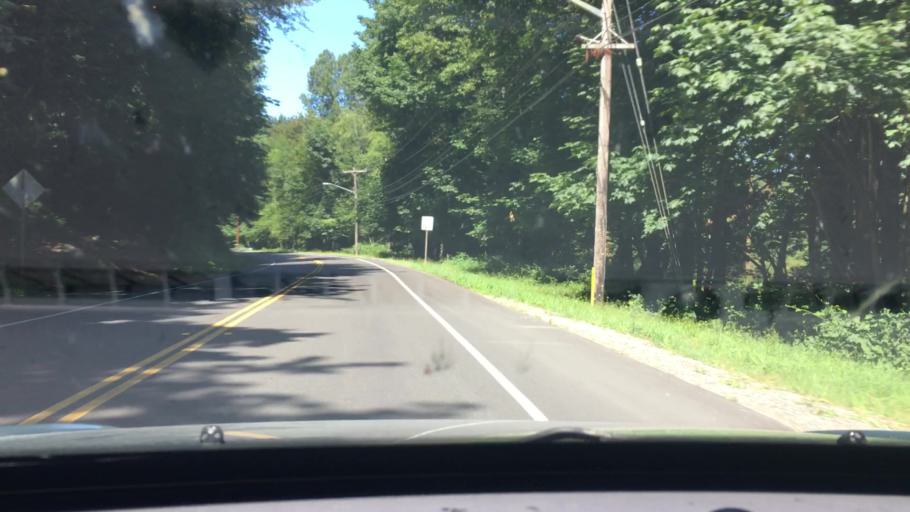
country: US
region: Washington
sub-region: King County
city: Newcastle
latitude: 47.5379
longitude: -122.1356
